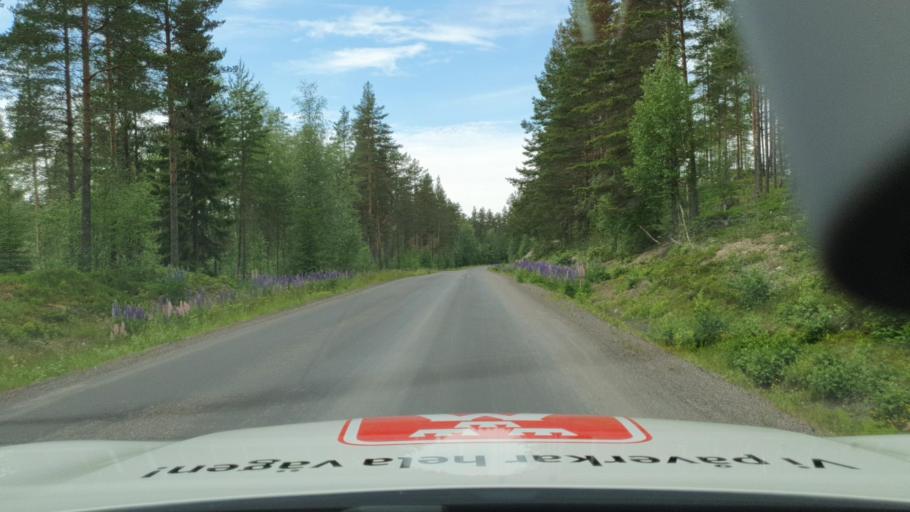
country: NO
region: Hedmark
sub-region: Grue
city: Kirkenaer
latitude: 60.6843
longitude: 12.6417
